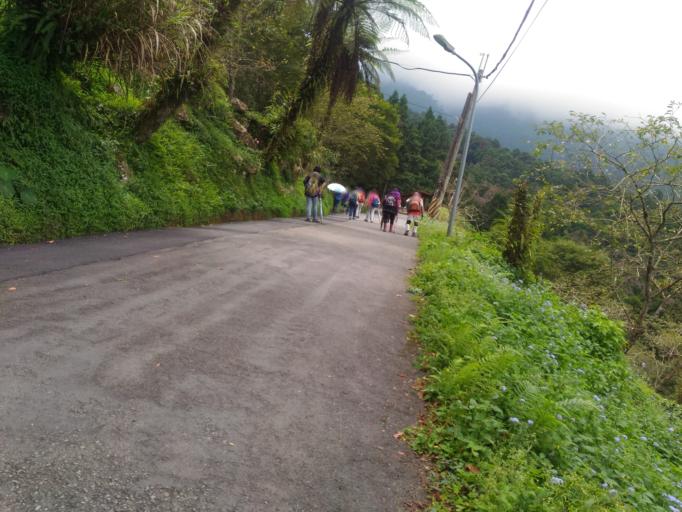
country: TW
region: Taiwan
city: Lugu
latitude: 23.6664
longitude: 120.7999
